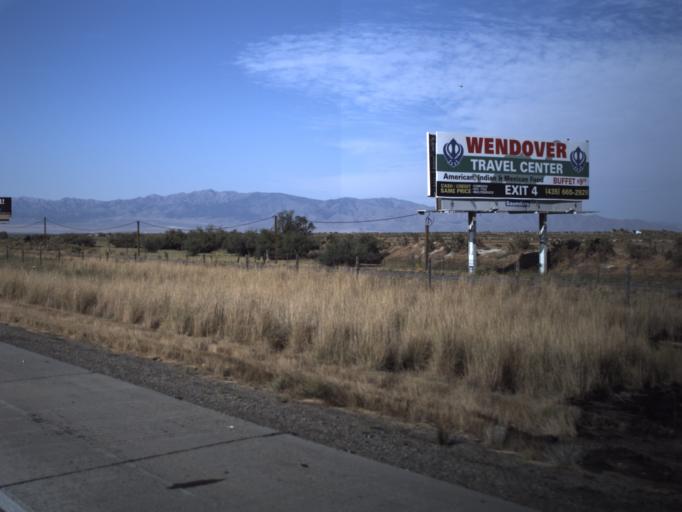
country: US
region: Utah
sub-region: Tooele County
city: Stansbury park
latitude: 40.6843
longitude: -112.2735
